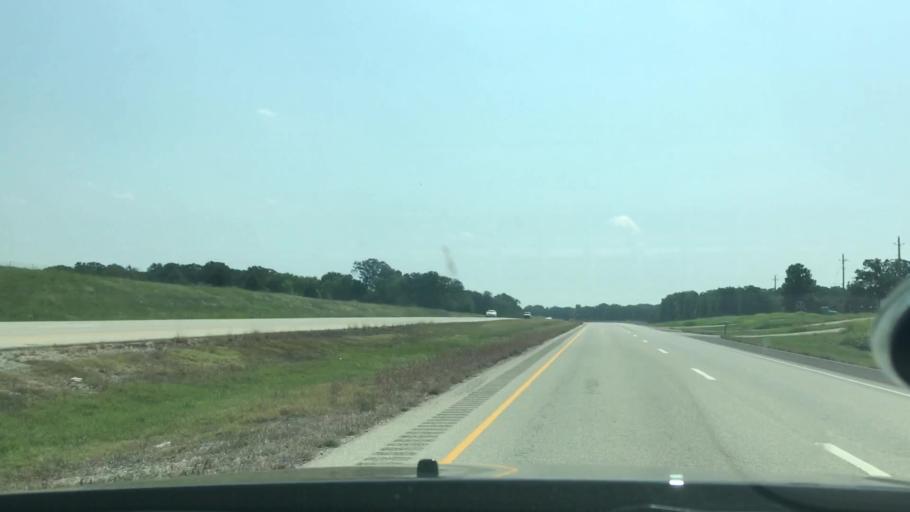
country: US
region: Oklahoma
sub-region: Atoka County
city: Atoka
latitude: 34.3218
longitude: -96.0386
